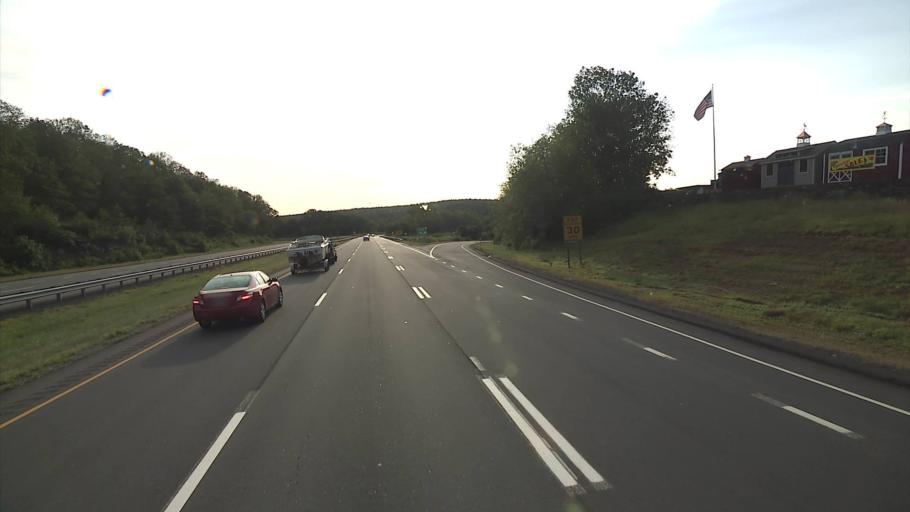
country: US
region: Connecticut
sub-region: New London County
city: Colchester
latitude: 41.5908
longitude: -72.4000
